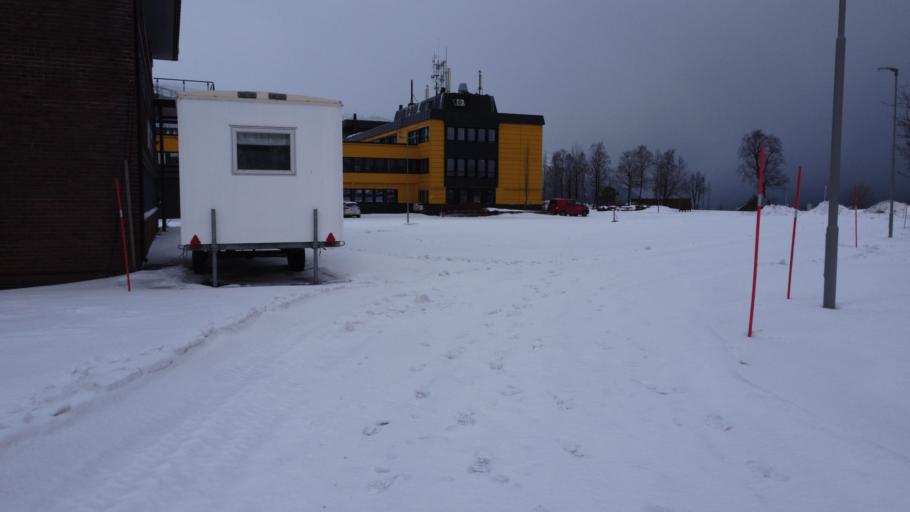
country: NO
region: Nordland
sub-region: Rana
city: Mo i Rana
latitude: 66.3142
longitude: 14.1592
